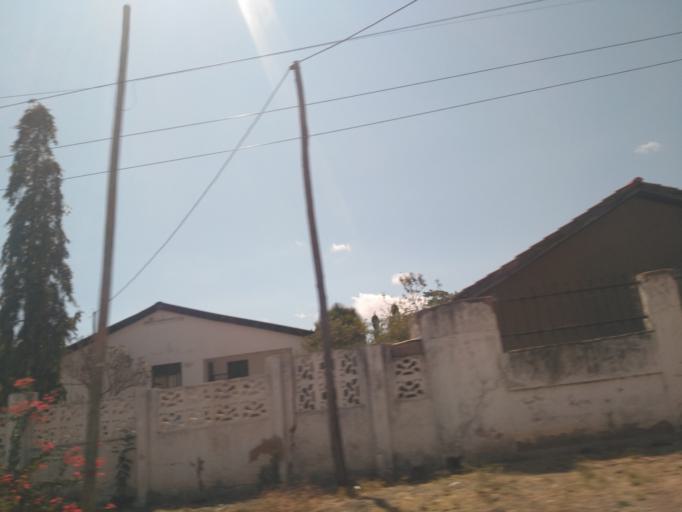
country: TZ
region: Dodoma
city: Dodoma
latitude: -6.1653
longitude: 35.7597
